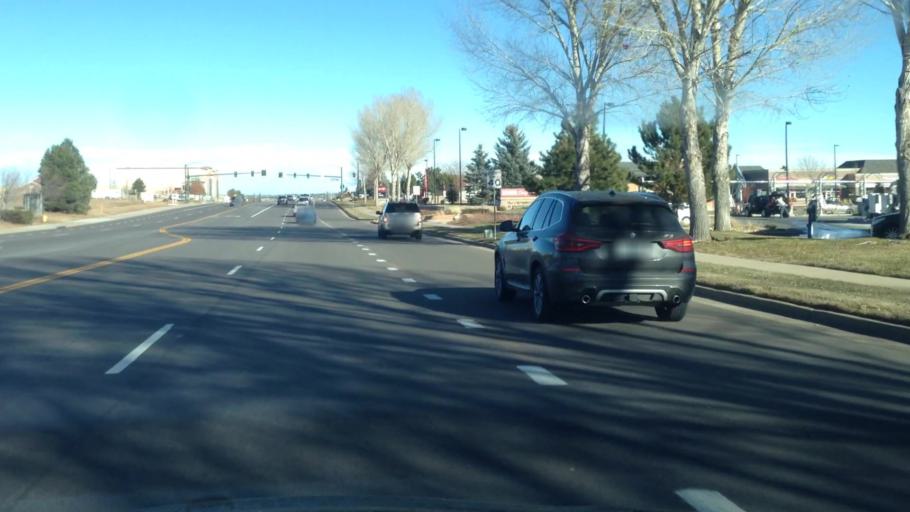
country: US
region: Colorado
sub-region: Douglas County
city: Stonegate
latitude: 39.5347
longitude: -104.7933
